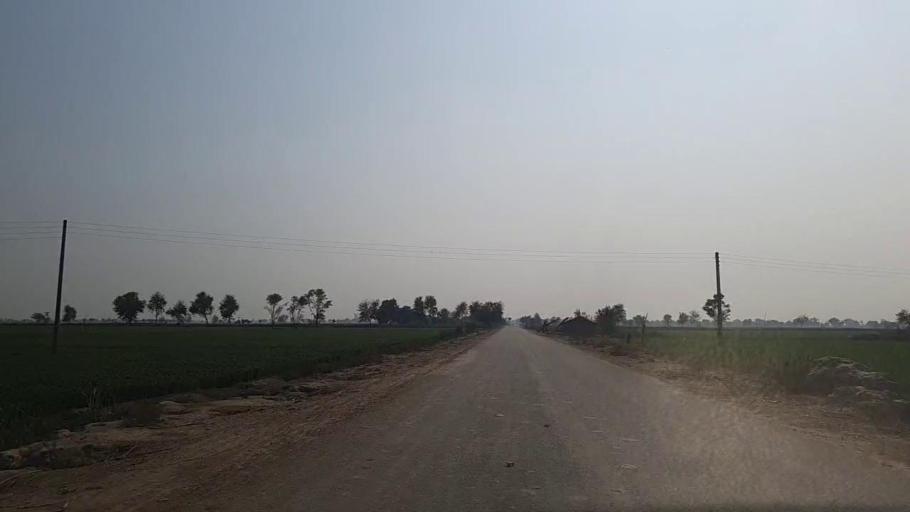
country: PK
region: Sindh
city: Jam Sahib
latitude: 26.3537
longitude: 68.5345
